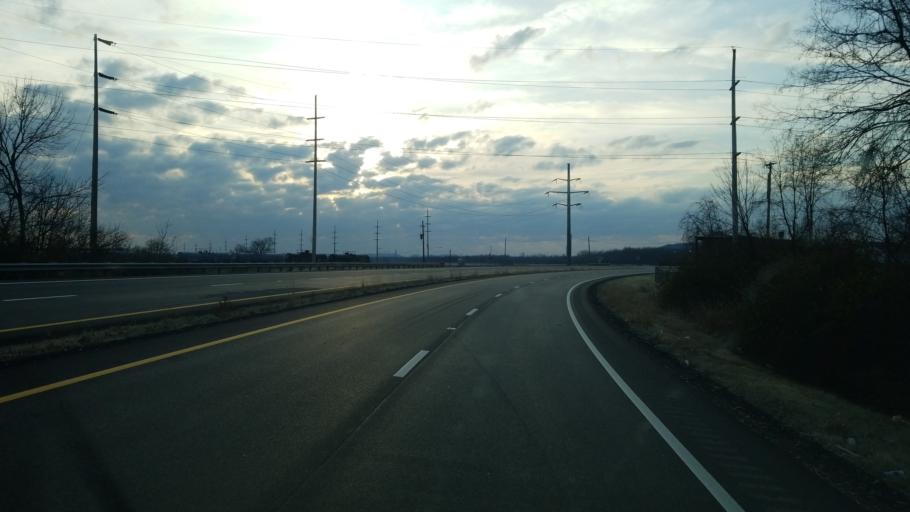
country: US
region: Ohio
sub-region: Ross County
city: Chillicothe
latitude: 39.3182
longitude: -82.9626
